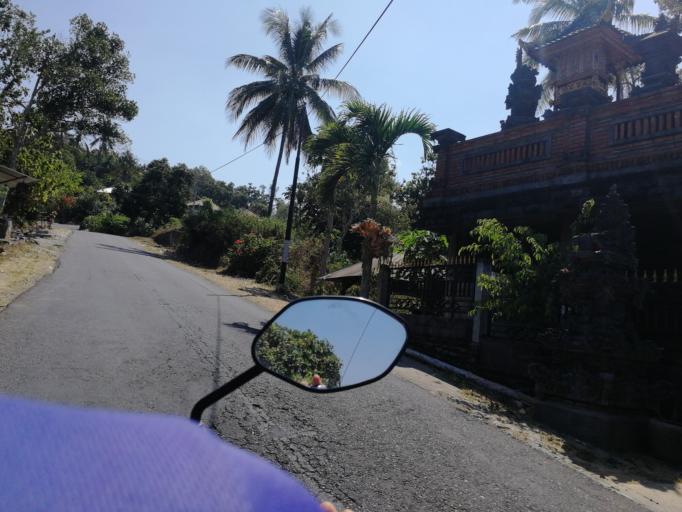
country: ID
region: Bali
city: Banjar Kedisan
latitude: -8.1449
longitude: 115.3093
